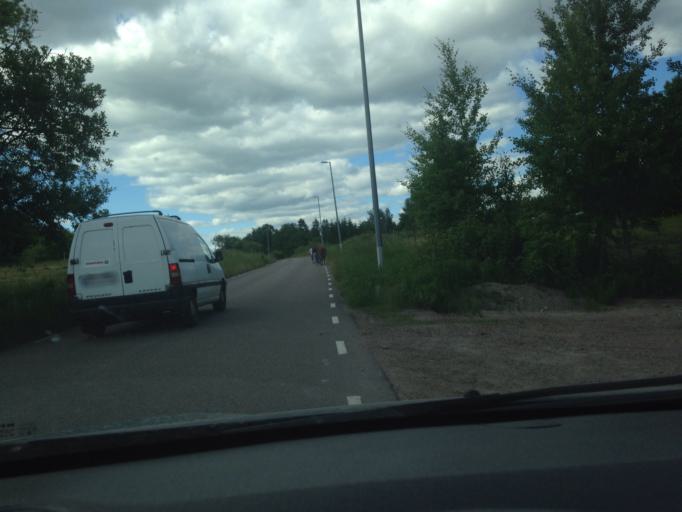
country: SE
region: Vaestra Goetaland
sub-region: Goteborg
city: Goeteborg
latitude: 57.7808
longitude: 11.9346
